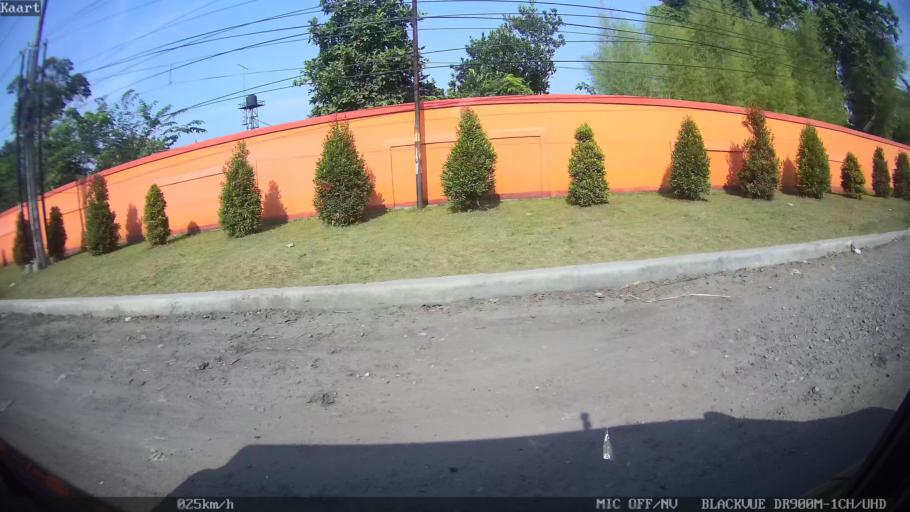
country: ID
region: Lampung
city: Natar
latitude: -5.2650
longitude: 105.1853
